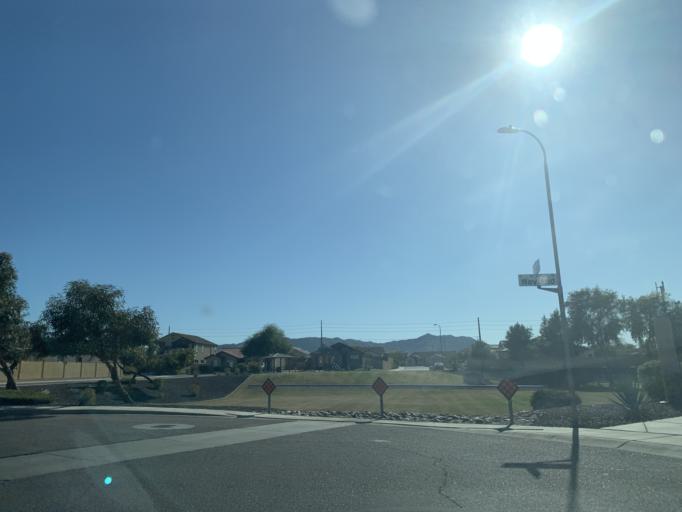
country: US
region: Arizona
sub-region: Maricopa County
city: Laveen
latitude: 33.3945
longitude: -112.1236
